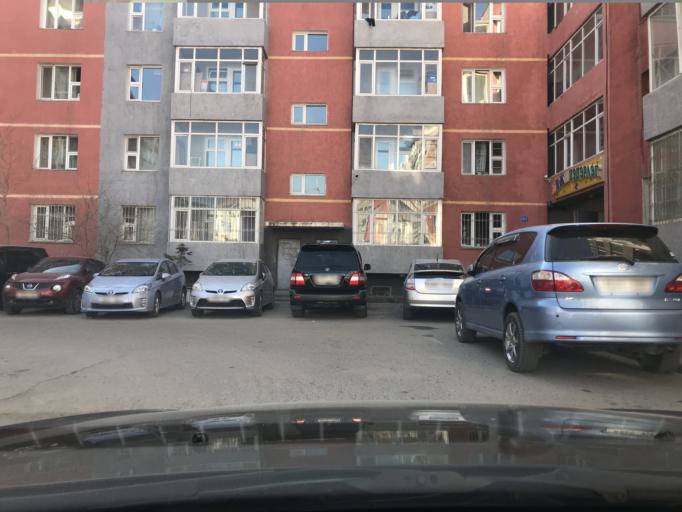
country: MN
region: Ulaanbaatar
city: Ulaanbaatar
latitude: 47.9103
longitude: 106.9406
